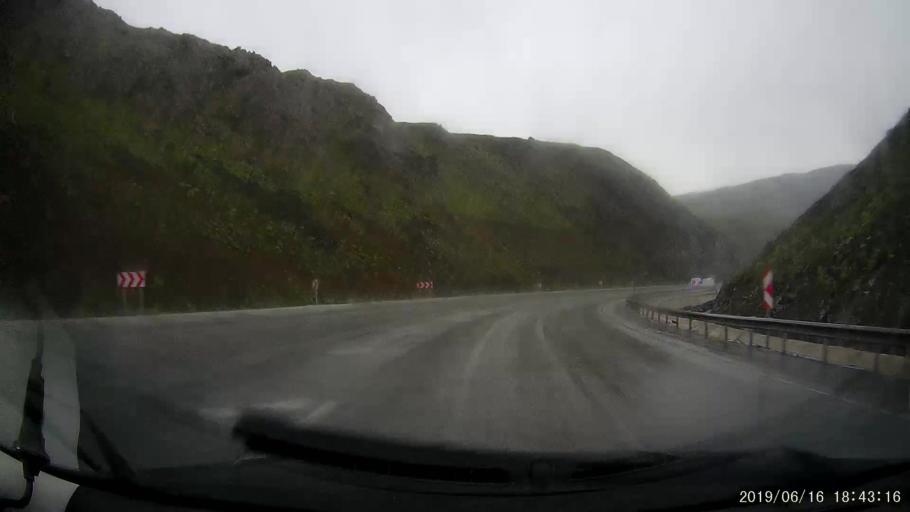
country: TR
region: Erzincan
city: Doganbeyli
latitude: 39.8678
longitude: 39.0927
